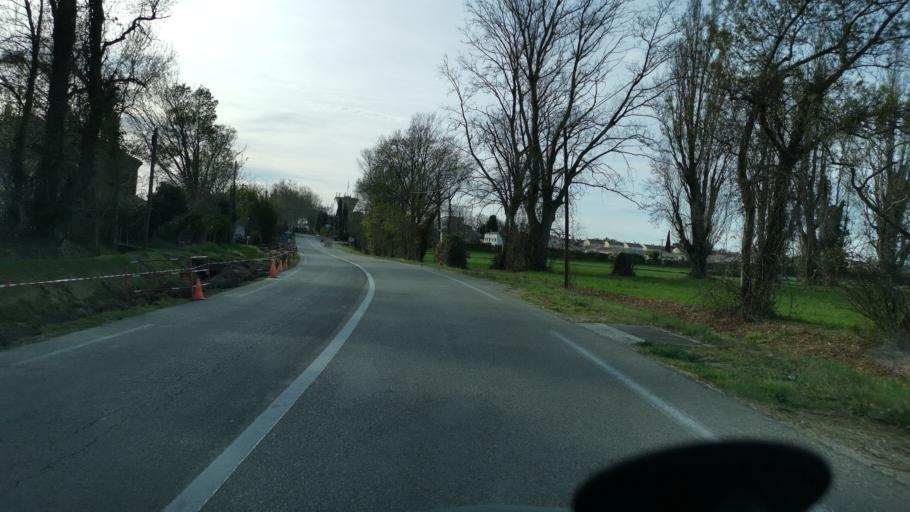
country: FR
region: Provence-Alpes-Cote d'Azur
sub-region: Departement des Bouches-du-Rhone
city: Saint-Martin-de-Crau
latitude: 43.6427
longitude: 4.7315
